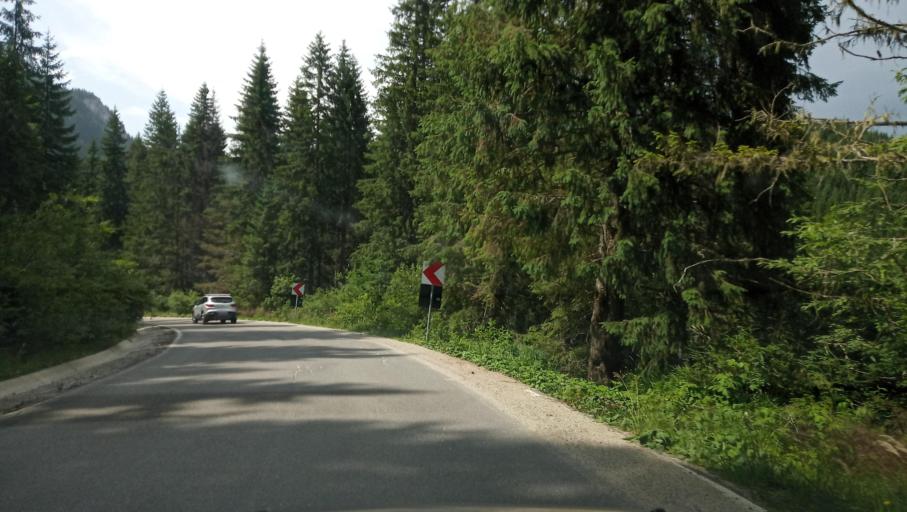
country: RO
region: Dambovita
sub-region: Comuna Moroeni
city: Glod
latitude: 45.3282
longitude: 25.4335
